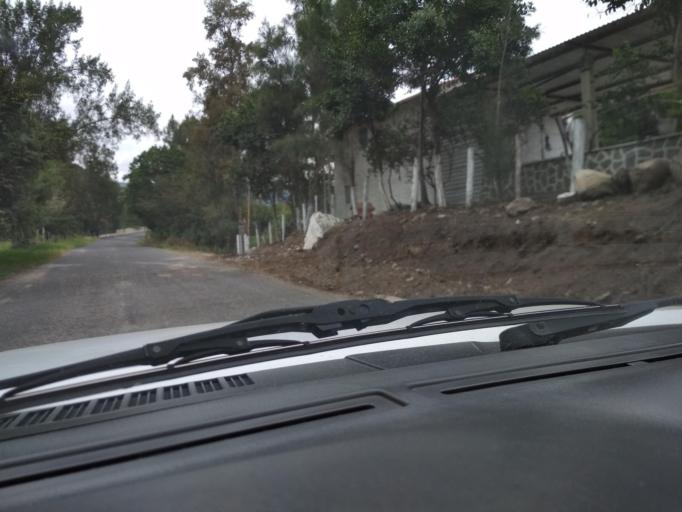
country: MX
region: Veracruz
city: Alto Lucero
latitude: 19.5959
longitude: -96.7942
